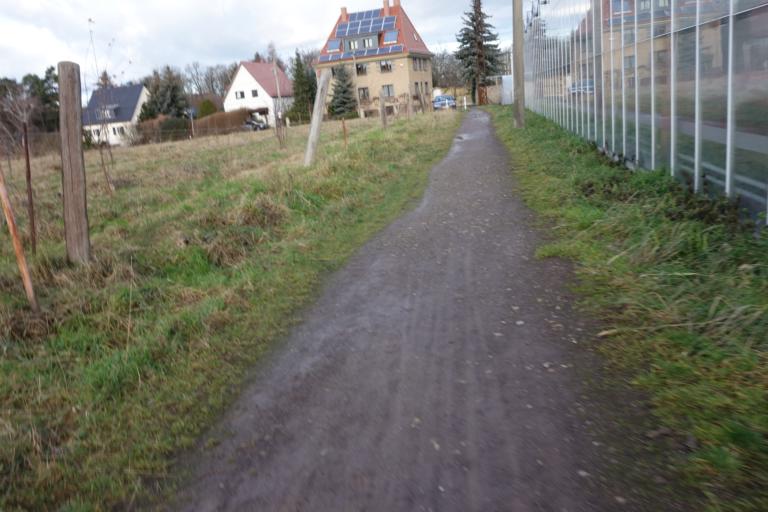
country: DE
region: Saxony
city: Radebeul
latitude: 51.0583
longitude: 13.6479
